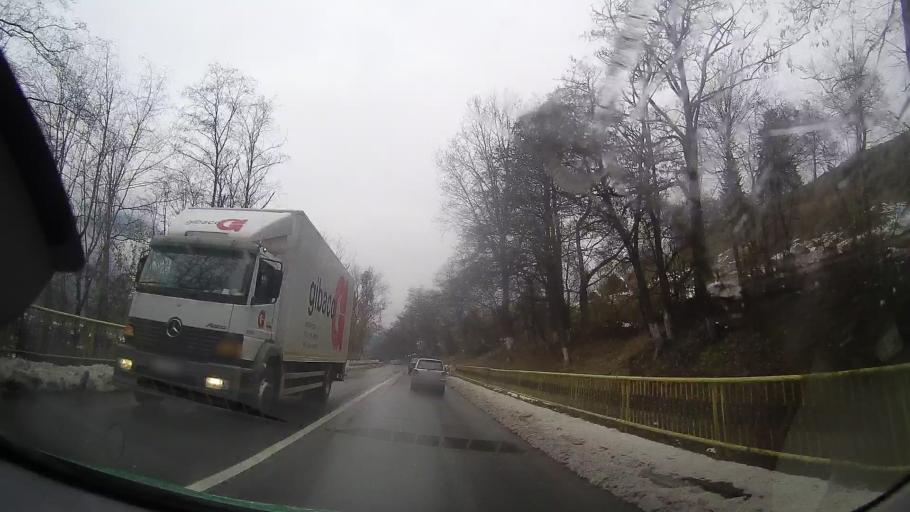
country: RO
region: Neamt
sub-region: Comuna Bicaz
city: Dodeni
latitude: 46.9022
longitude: 26.1158
